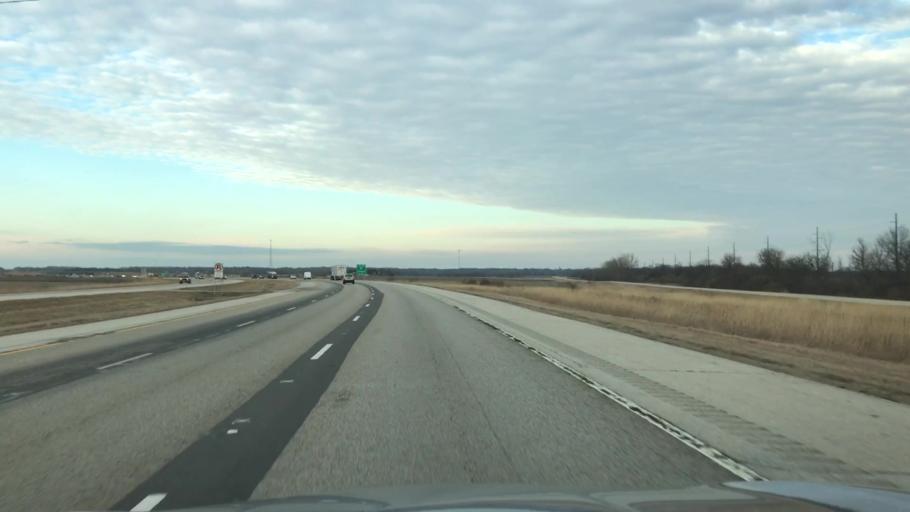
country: US
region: Illinois
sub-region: Logan County
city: Lincoln
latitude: 40.0994
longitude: -89.4174
